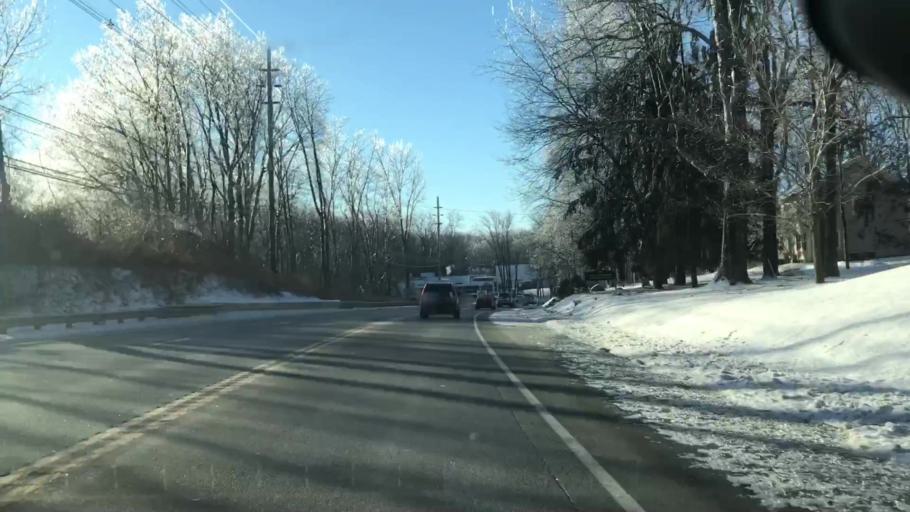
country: US
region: New Jersey
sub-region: Morris County
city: Netcong
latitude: 40.8765
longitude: -74.6922
